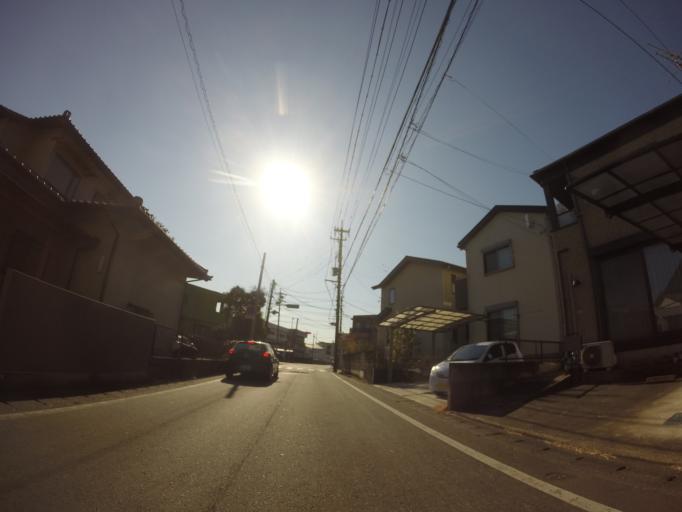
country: JP
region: Shizuoka
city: Shizuoka-shi
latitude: 35.0099
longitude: 138.3851
